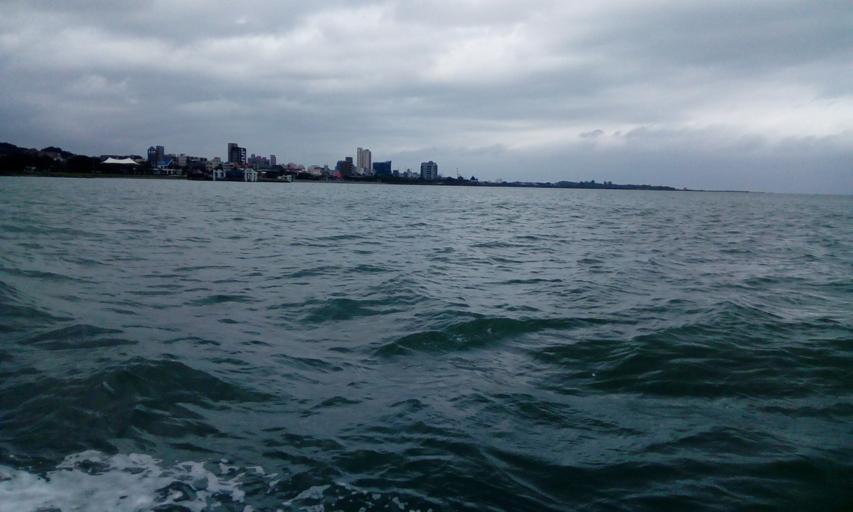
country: TW
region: Taipei
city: Taipei
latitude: 25.1625
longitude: 121.4364
